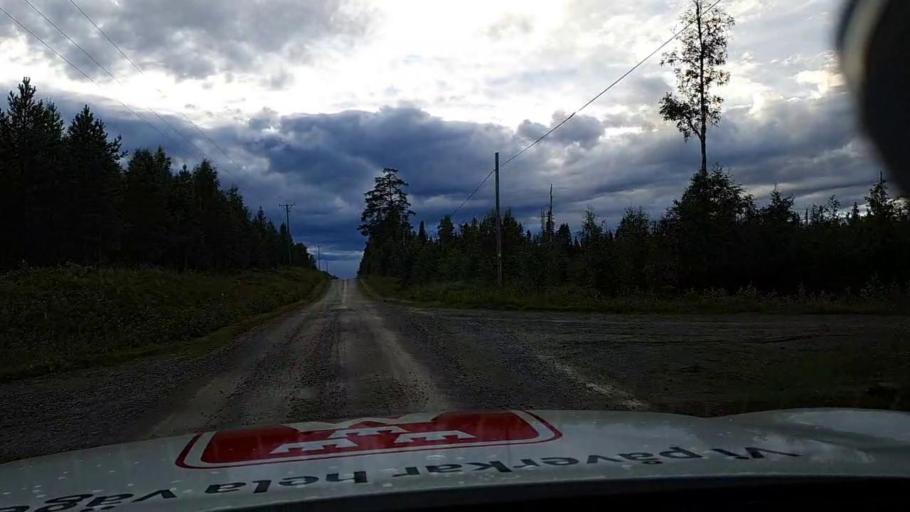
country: SE
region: Jaemtland
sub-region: Bergs Kommun
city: Hoverberg
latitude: 62.8854
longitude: 14.5829
